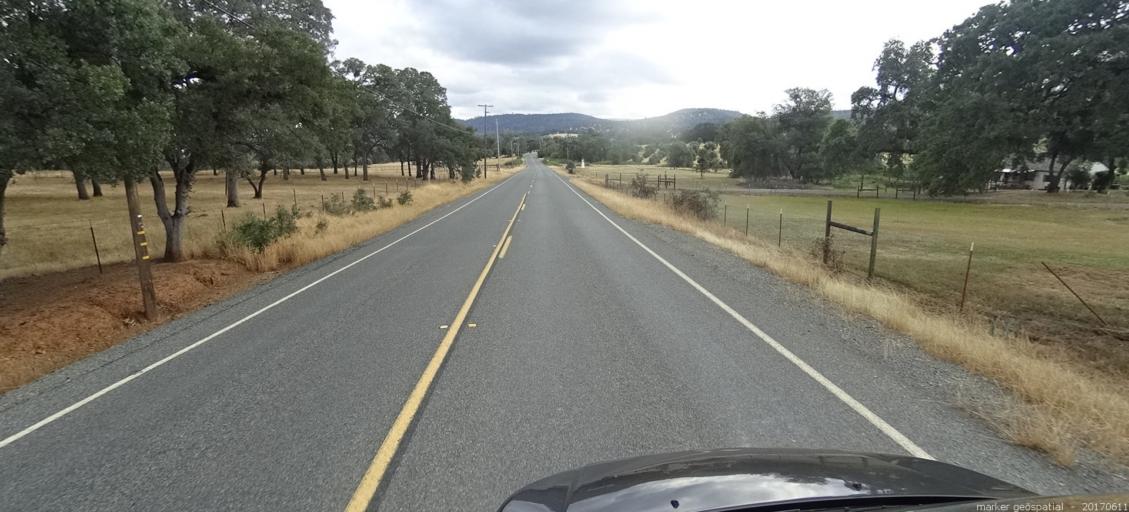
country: US
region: California
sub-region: Yuba County
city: Loma Rica
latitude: 39.3826
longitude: -121.4103
